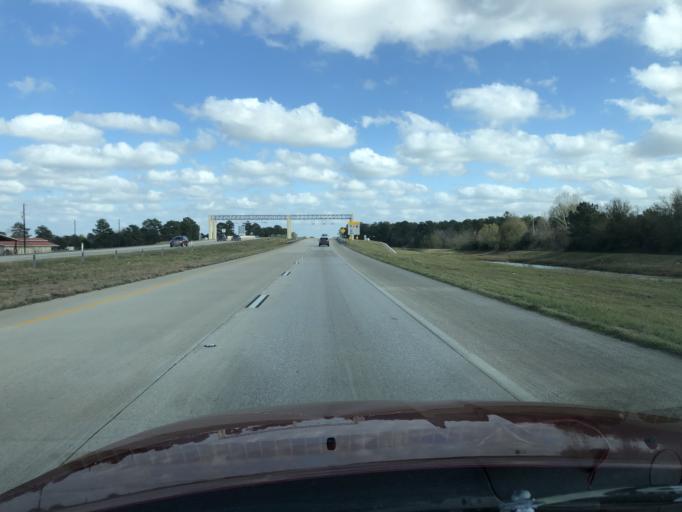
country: US
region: Texas
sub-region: Harris County
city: Tomball
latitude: 30.0521
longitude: -95.6417
